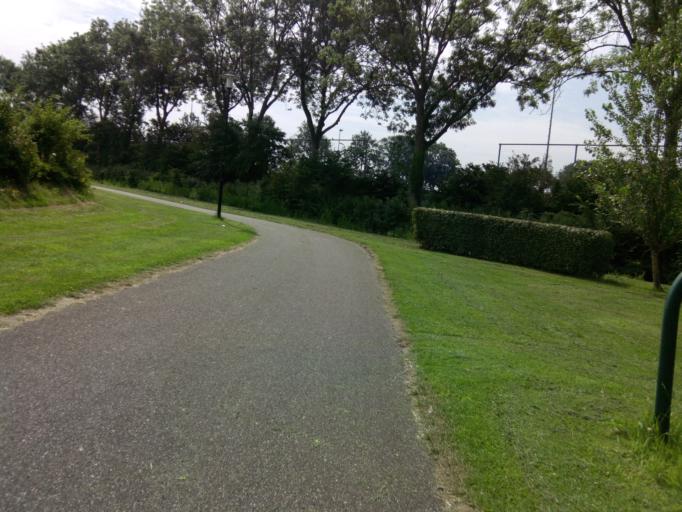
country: NL
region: Utrecht
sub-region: Gemeente Bunschoten
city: Bunschoten
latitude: 52.2583
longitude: 5.3802
